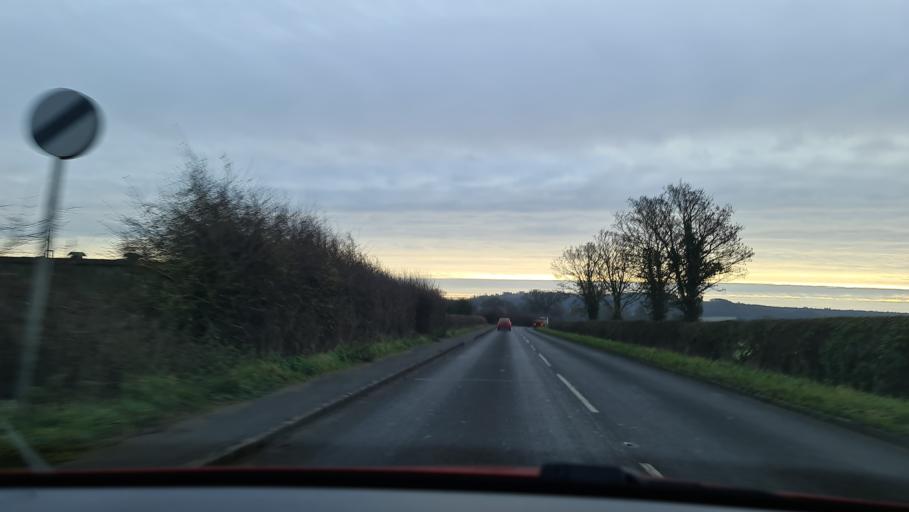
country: GB
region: England
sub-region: Buckinghamshire
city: Princes Risborough
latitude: 51.7340
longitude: -0.8484
